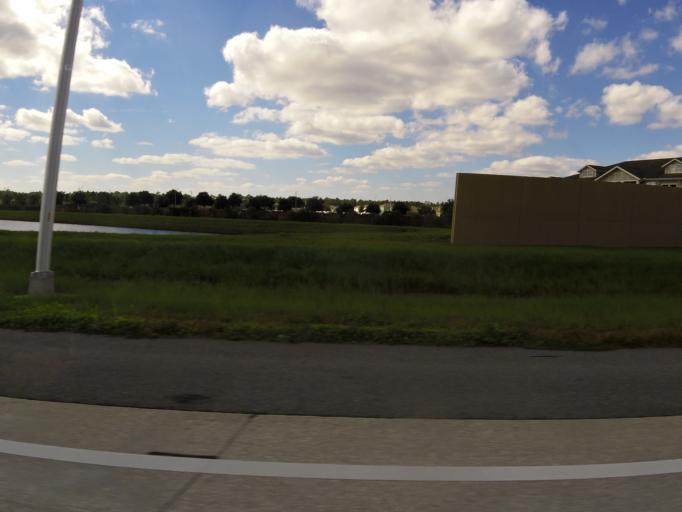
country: US
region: Florida
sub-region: Saint Johns County
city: Fruit Cove
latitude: 30.1123
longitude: -81.5151
